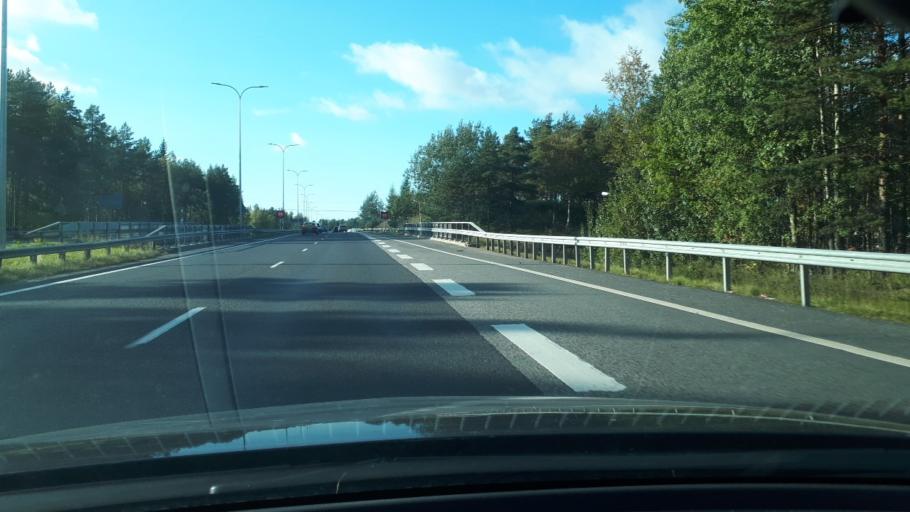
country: FI
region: Northern Ostrobothnia
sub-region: Oulu
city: Oulu
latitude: 65.0304
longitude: 25.5003
